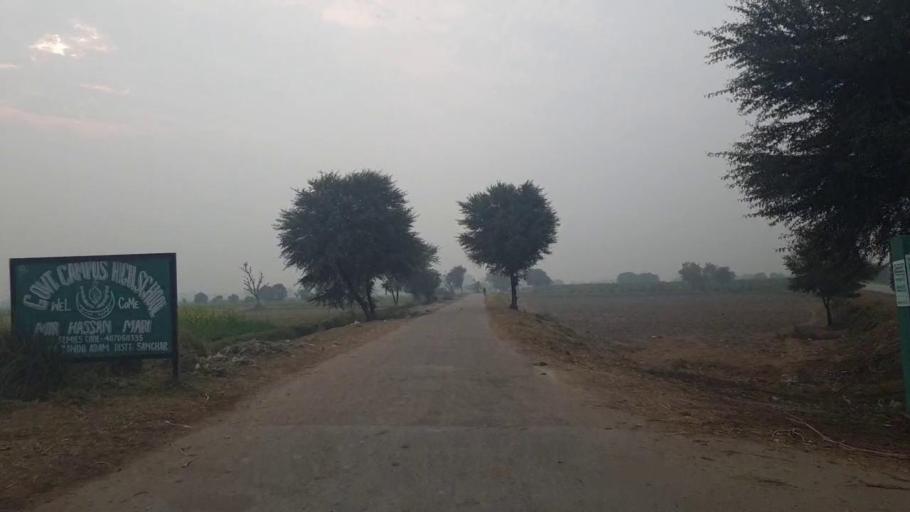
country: PK
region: Sindh
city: Tando Adam
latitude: 25.7382
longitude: 68.6690
